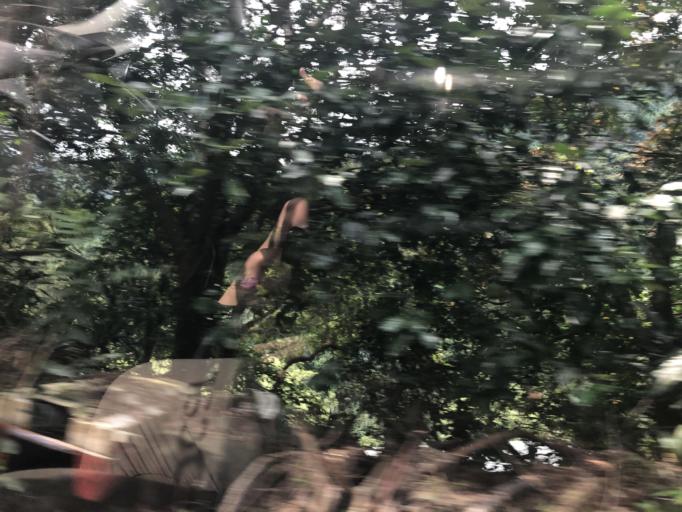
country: TW
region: Taiwan
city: Daxi
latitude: 24.8706
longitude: 121.4086
